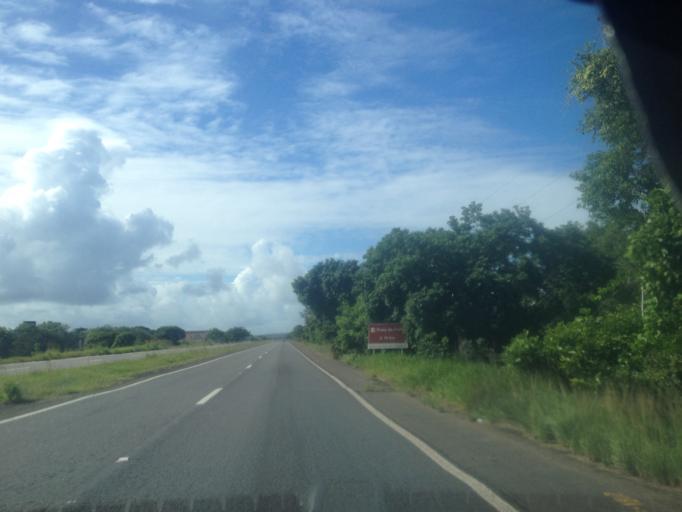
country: BR
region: Bahia
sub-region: Mata De Sao Joao
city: Mata de Sao Joao
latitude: -12.6353
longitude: -38.0682
